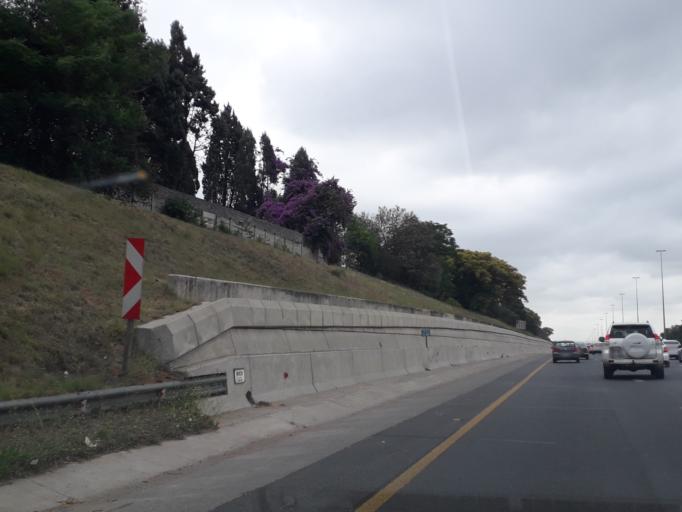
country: ZA
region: Gauteng
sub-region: City of Johannesburg Metropolitan Municipality
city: Roodepoort
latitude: -26.1098
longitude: 27.9581
